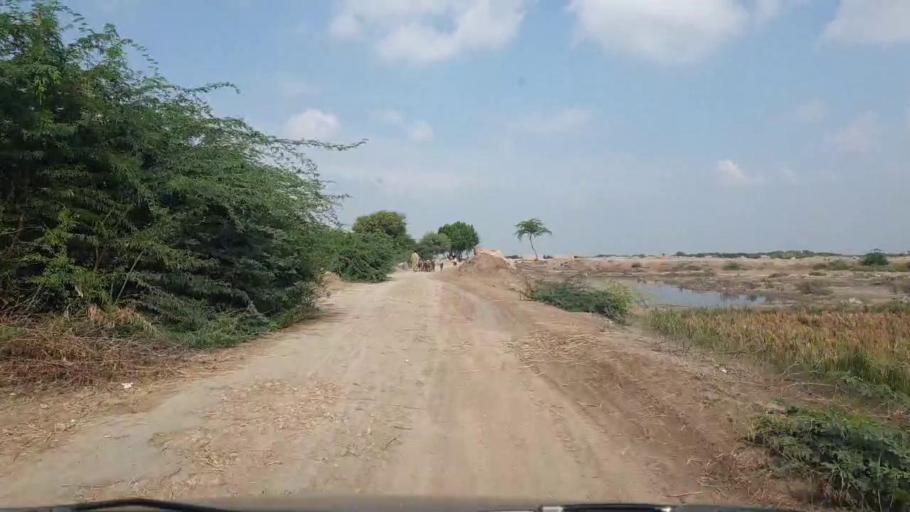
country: PK
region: Sindh
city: Badin
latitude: 24.4714
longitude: 68.5902
